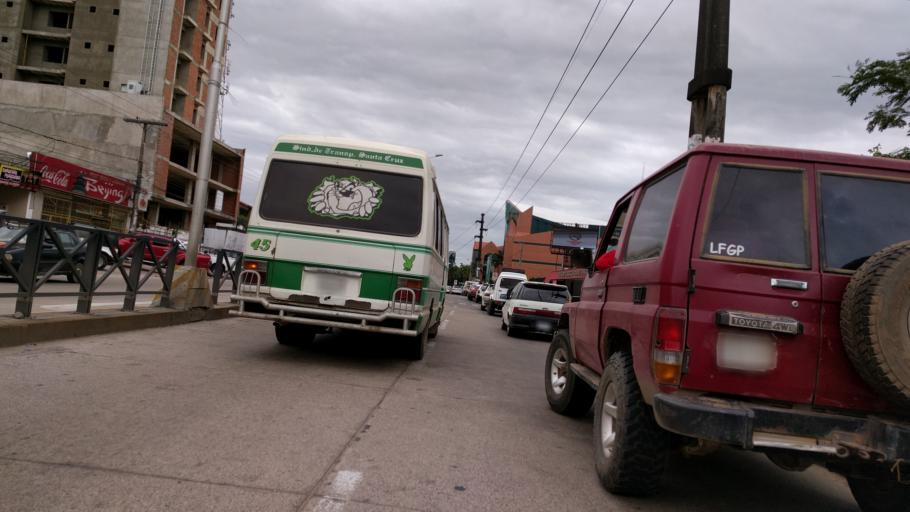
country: BO
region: Santa Cruz
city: Santa Cruz de la Sierra
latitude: -17.7677
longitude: -63.2002
